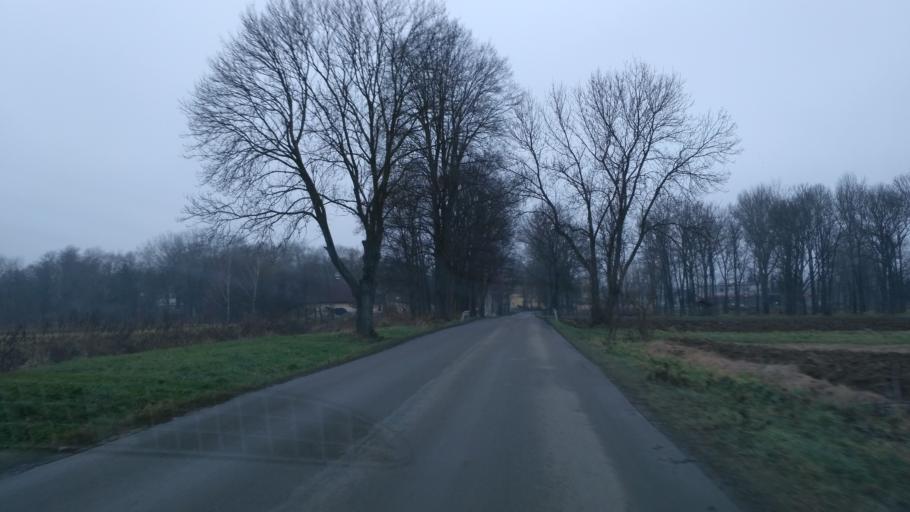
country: PL
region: Subcarpathian Voivodeship
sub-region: Powiat przeworski
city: Zarzecze
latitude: 49.9839
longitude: 22.5477
